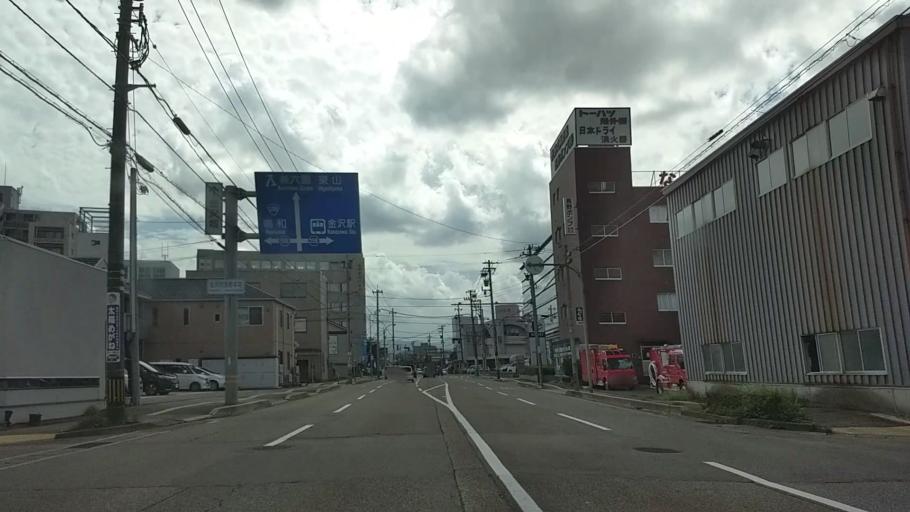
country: JP
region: Ishikawa
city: Kanazawa-shi
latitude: 36.5840
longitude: 136.6633
